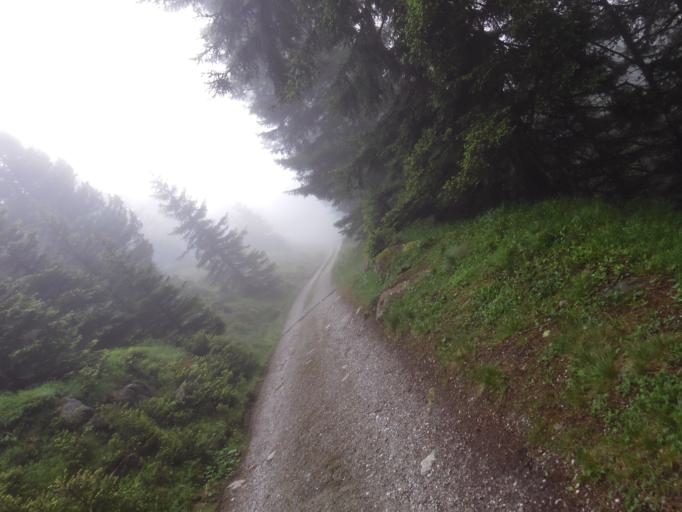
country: AT
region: Tyrol
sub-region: Politischer Bezirk Innsbruck Land
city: Neustift im Stubaital
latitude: 47.0529
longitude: 11.2211
